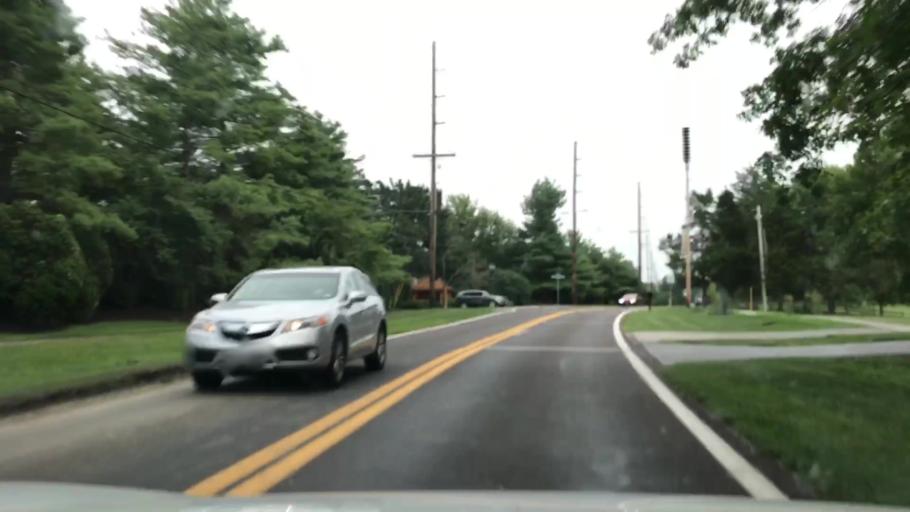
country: US
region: Missouri
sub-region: Saint Louis County
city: Clarkson Valley
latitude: 38.6315
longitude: -90.6001
